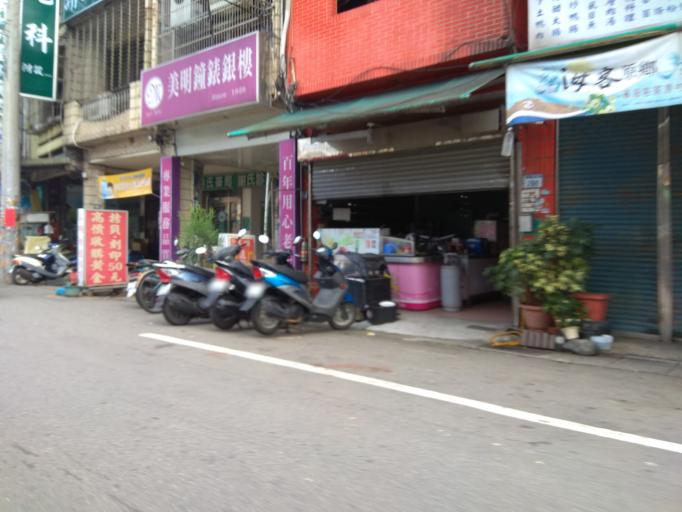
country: TW
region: Taiwan
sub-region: Hsinchu
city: Zhubei
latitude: 24.9732
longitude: 121.1069
